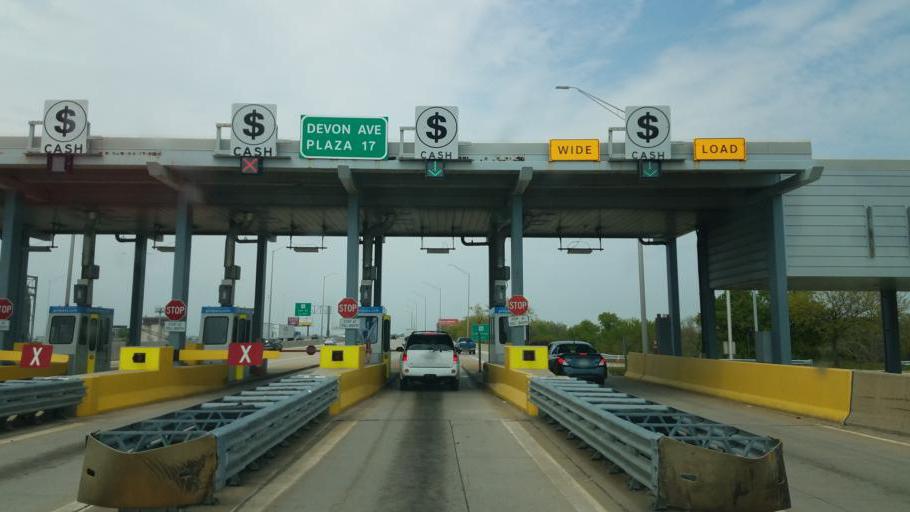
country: US
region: Illinois
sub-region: Cook County
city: Rosemont
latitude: 41.9986
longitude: -87.8778
